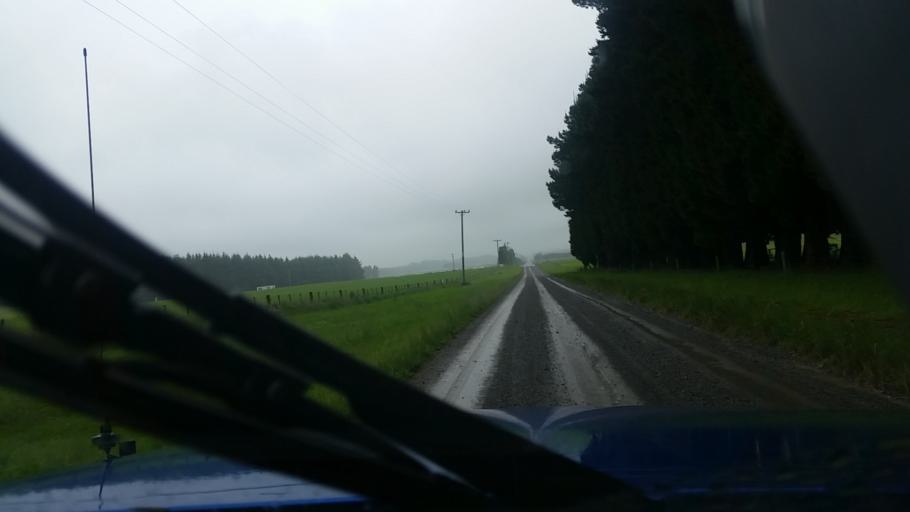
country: NZ
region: Canterbury
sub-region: Ashburton District
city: Methven
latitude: -43.5671
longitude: 171.5478
